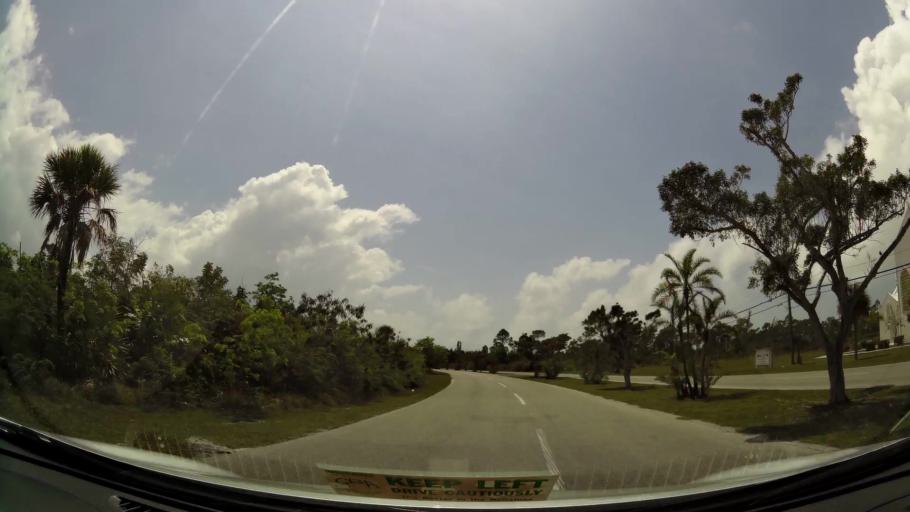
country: BS
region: Freeport
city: Lucaya
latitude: 26.5247
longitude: -78.6299
